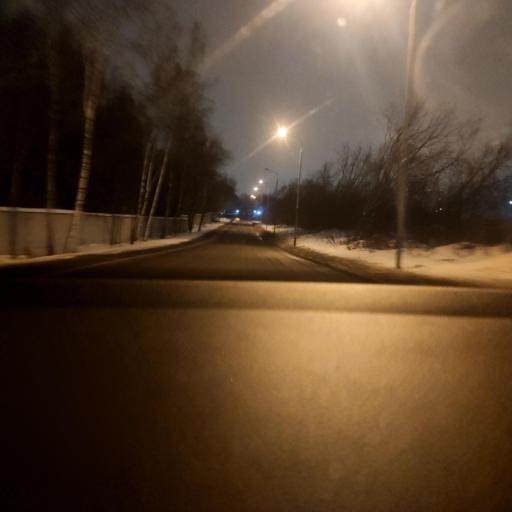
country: RU
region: Moskovskaya
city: Vostryakovo
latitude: 55.6601
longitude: 37.4524
